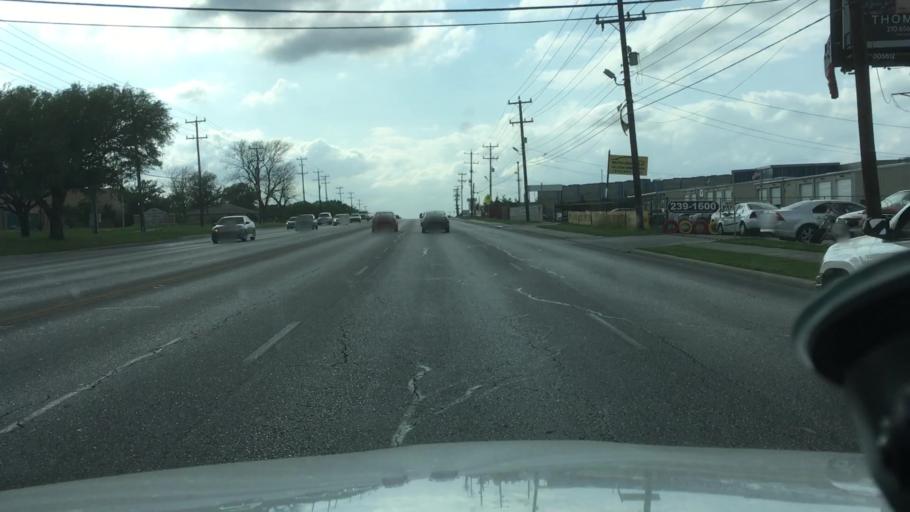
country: US
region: Texas
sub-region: Bexar County
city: Windcrest
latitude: 29.5018
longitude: -98.3597
